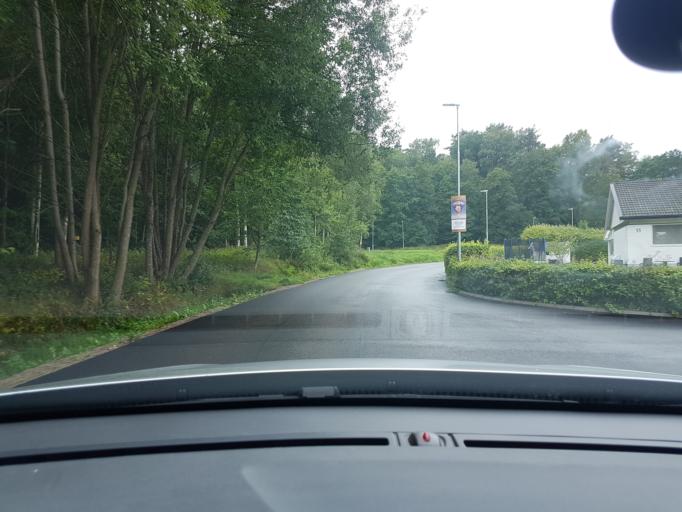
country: SE
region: Vaestra Goetaland
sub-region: Ale Kommun
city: Salanda
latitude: 57.9809
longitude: 12.2200
